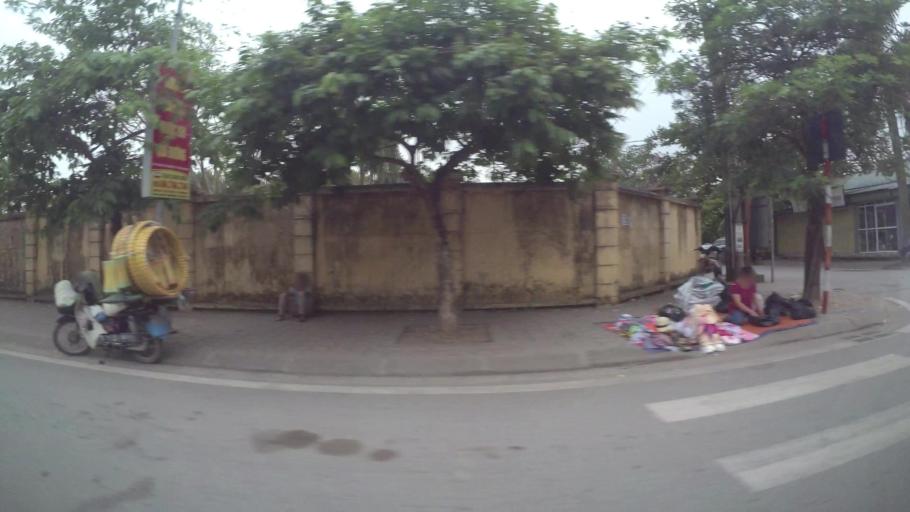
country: VN
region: Ha Noi
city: Hoan Kiem
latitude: 21.0603
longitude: 105.8886
